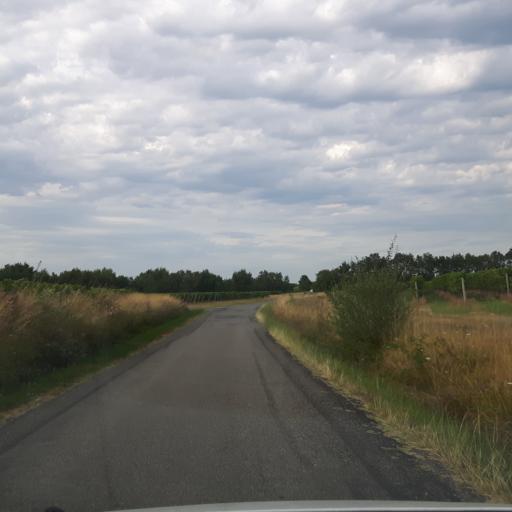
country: FR
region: Midi-Pyrenees
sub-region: Departement de la Haute-Garonne
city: Castelnau-d'Estretefonds
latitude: 43.8180
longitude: 1.3604
